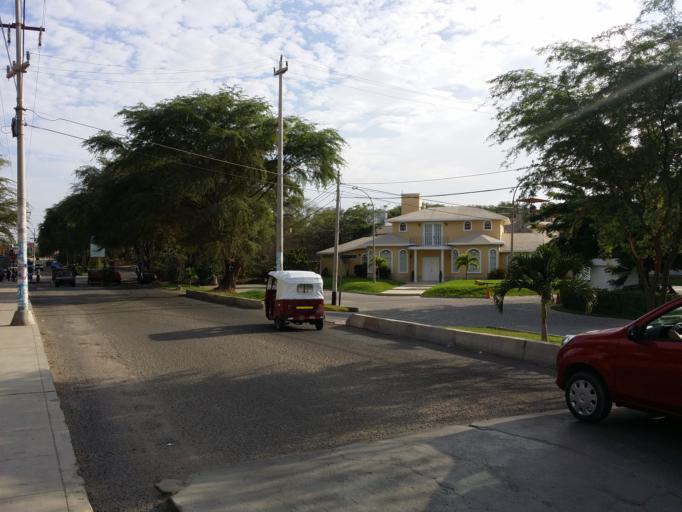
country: PE
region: Piura
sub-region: Provincia de Piura
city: Piura
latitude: -5.1733
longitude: -80.6277
